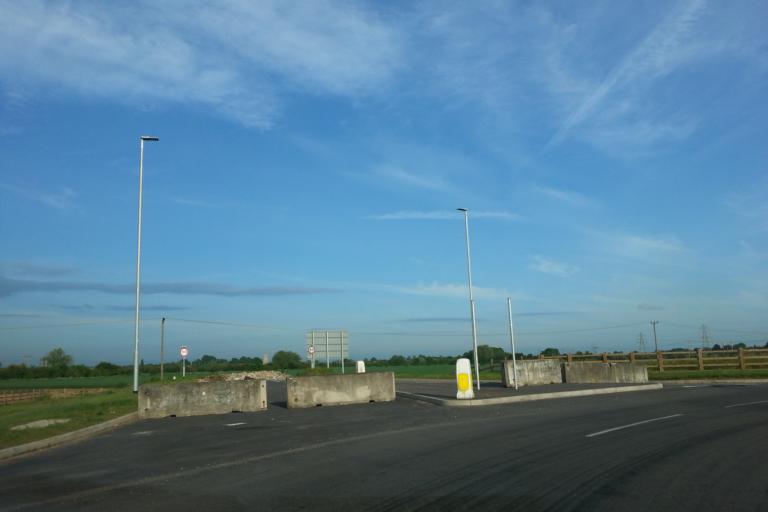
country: GB
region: England
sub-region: Nottinghamshire
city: Newark on Trent
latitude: 53.0524
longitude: -0.8068
